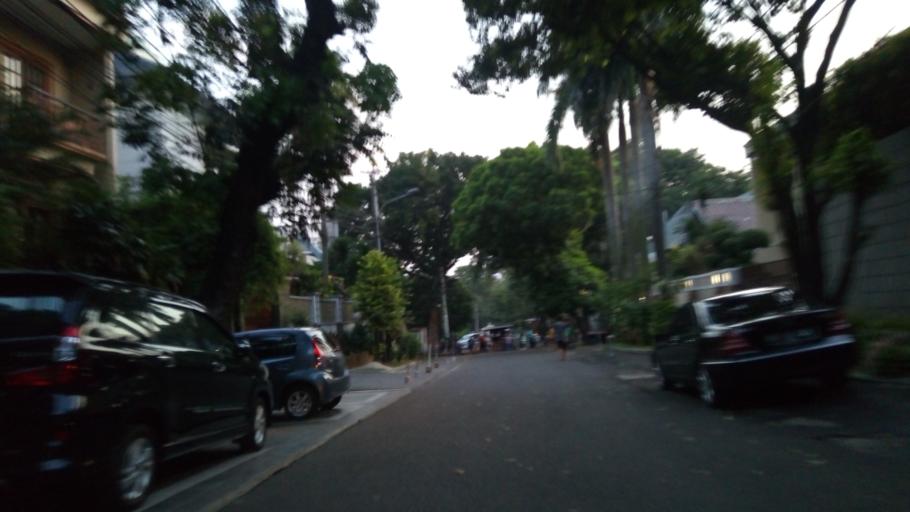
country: ID
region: Jakarta Raya
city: Jakarta
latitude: -6.2441
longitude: 106.7953
